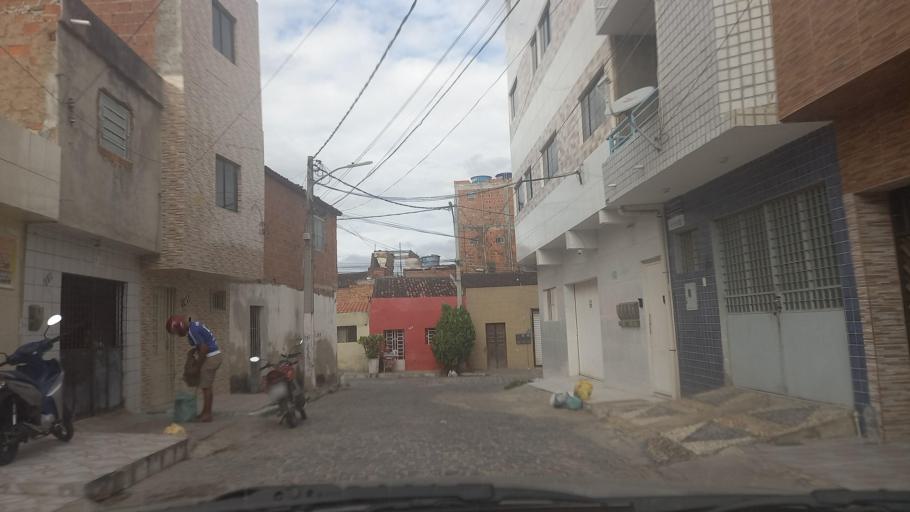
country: BR
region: Pernambuco
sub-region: Caruaru
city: Caruaru
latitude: -8.2916
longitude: -35.9766
